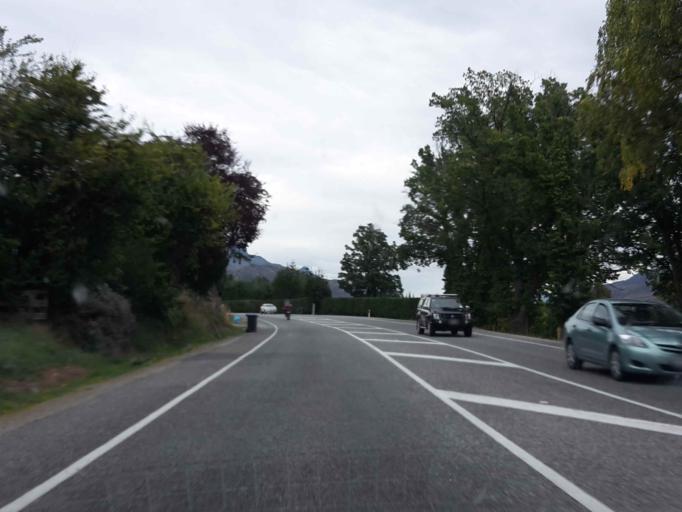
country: NZ
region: Otago
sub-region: Queenstown-Lakes District
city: Arrowtown
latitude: -44.9910
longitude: 168.8088
